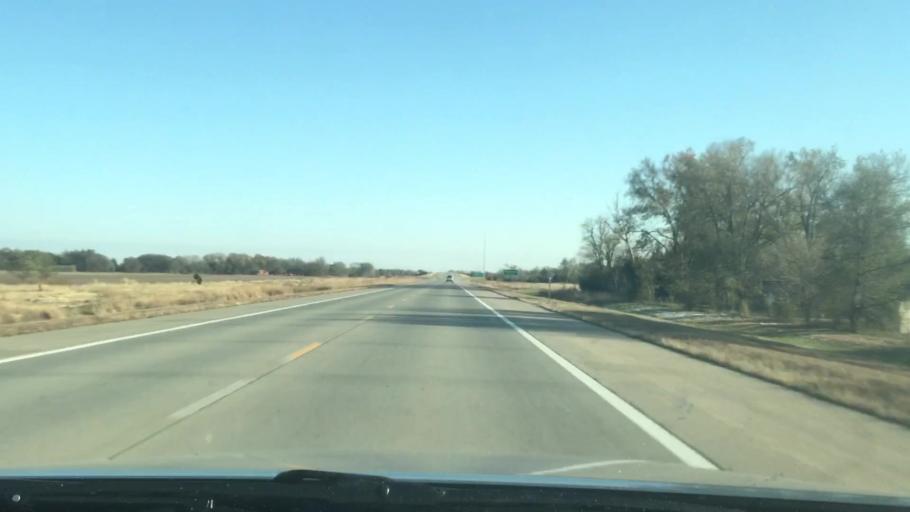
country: US
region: Kansas
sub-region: Reno County
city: Hutchinson
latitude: 38.0982
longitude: -98.0069
